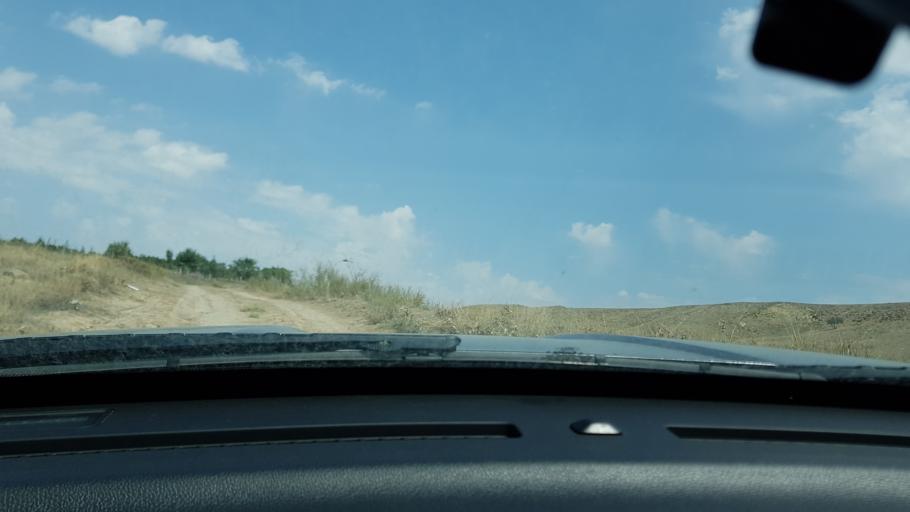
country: TM
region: Ahal
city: Baharly
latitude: 38.4070
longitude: 56.9100
